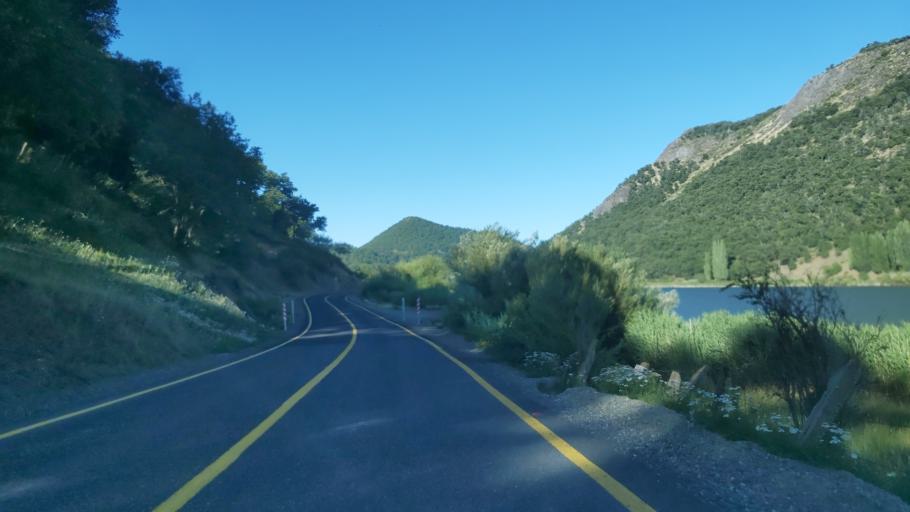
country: AR
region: Neuquen
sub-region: Departamento de Loncopue
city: Loncopue
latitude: -38.4403
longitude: -71.3358
